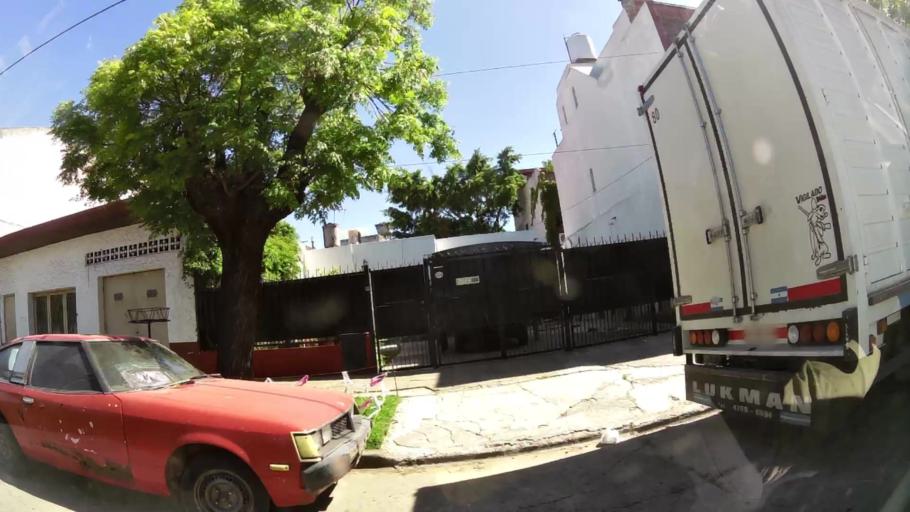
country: AR
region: Buenos Aires
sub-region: Partido de General San Martin
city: General San Martin
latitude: -34.5535
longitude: -58.5677
